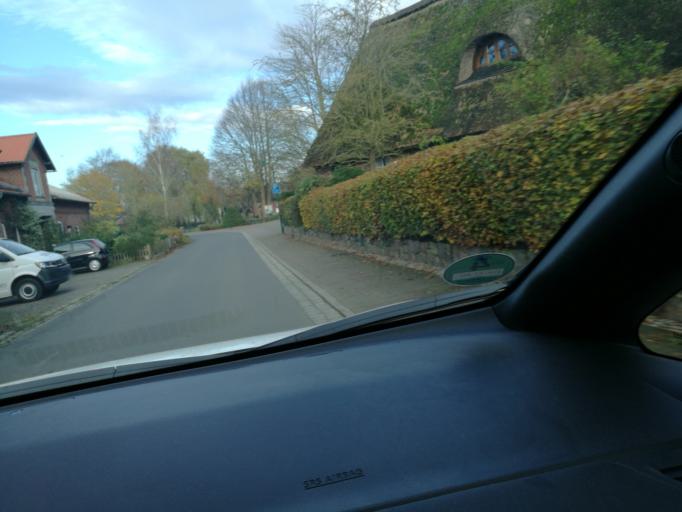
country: DE
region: Schleswig-Holstein
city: Bunsdorf
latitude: 54.3685
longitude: 9.7427
